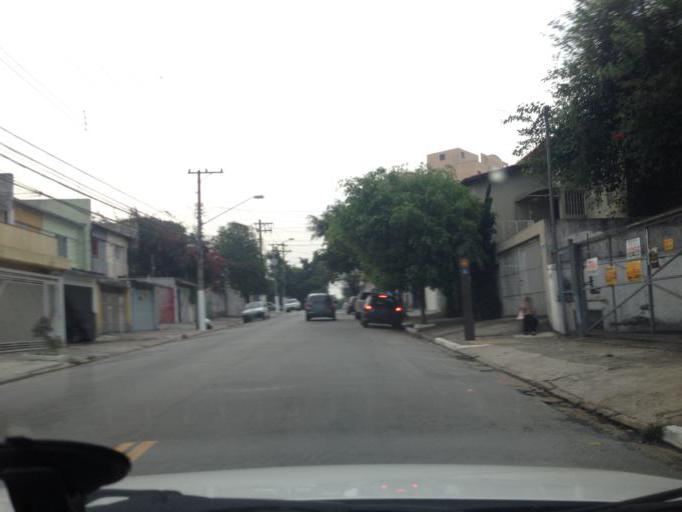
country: BR
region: Sao Paulo
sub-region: Osasco
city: Osasco
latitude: -23.5316
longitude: -46.7193
